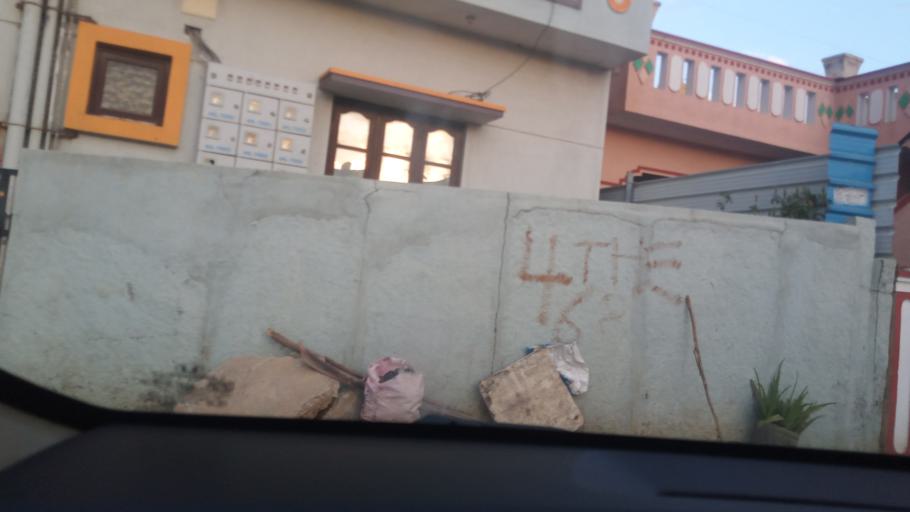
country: IN
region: Karnataka
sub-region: Bangalore Rural
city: Hoskote
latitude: 12.9791
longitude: 77.8012
